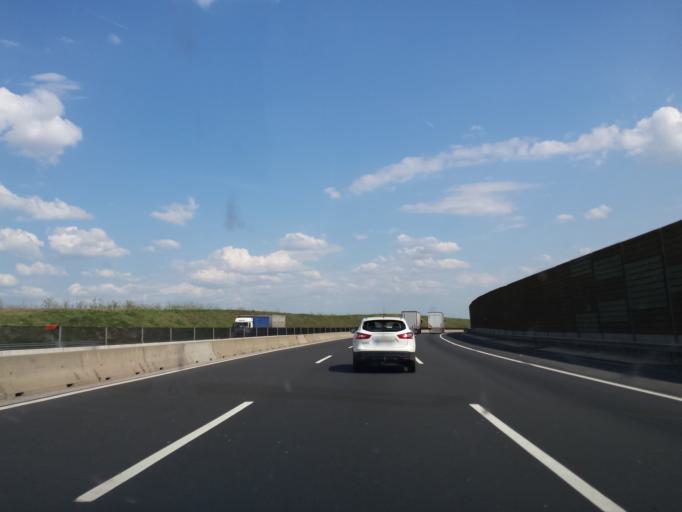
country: HU
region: Pest
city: Diosd
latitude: 47.4205
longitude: 18.9461
